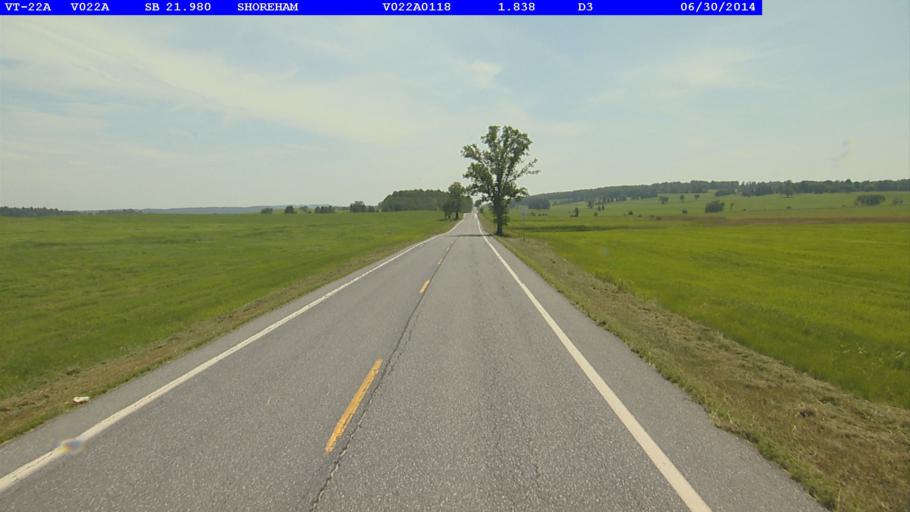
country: US
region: New York
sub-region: Essex County
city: Ticonderoga
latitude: 43.8759
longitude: -73.3096
